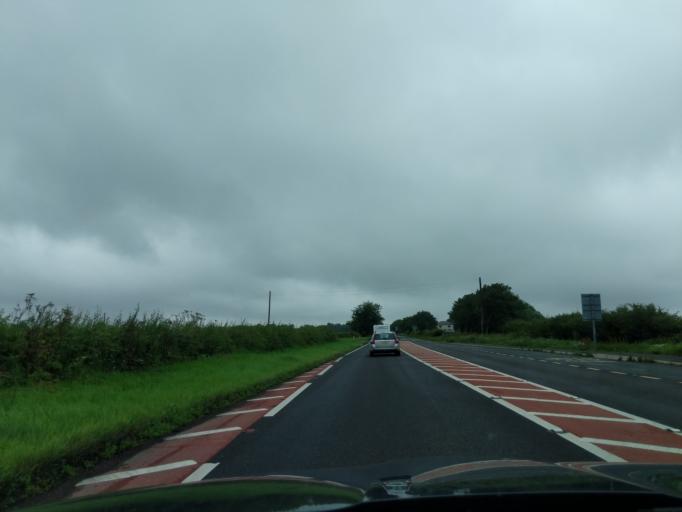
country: GB
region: England
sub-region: Northumberland
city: Hebron
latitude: 55.2257
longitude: -1.7057
